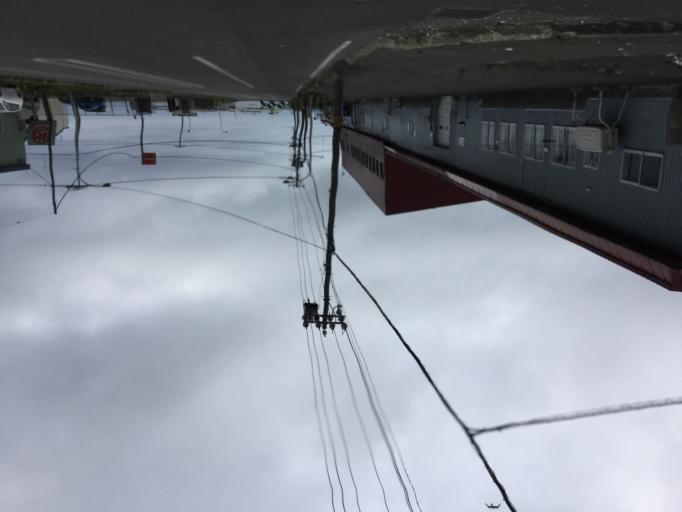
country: JP
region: Hokkaido
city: Wakkanai
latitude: 45.4078
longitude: 141.6823
